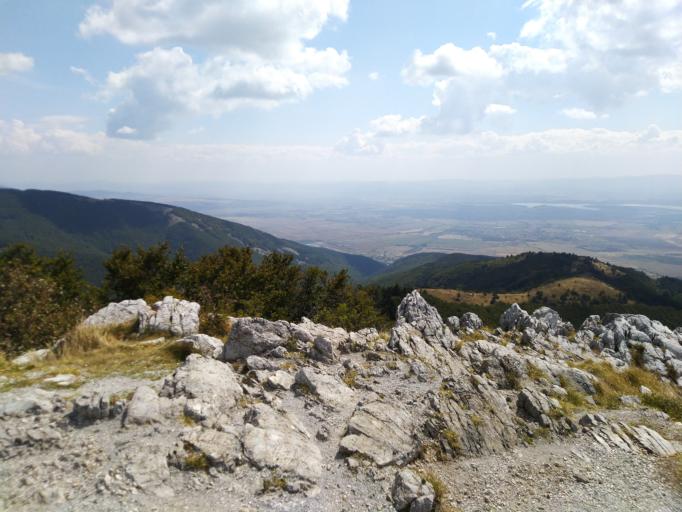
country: BG
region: Stara Zagora
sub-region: Obshtina Kazanluk
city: Shipka
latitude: 42.7466
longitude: 25.3224
